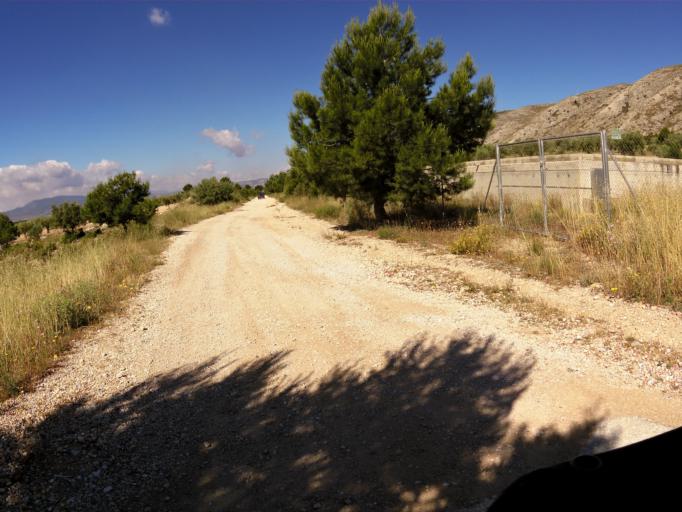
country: ES
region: Valencia
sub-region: Provincia de Alicante
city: Villena
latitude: 38.6356
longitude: -0.8334
